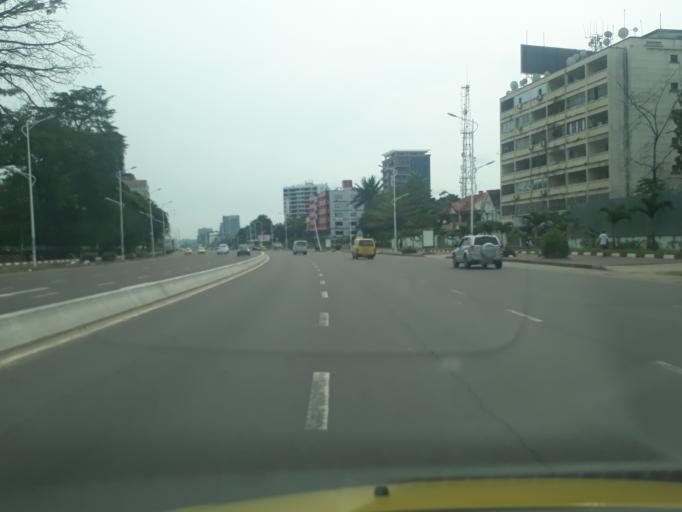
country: CD
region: Kinshasa
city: Kinshasa
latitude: -4.3072
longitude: 15.2944
